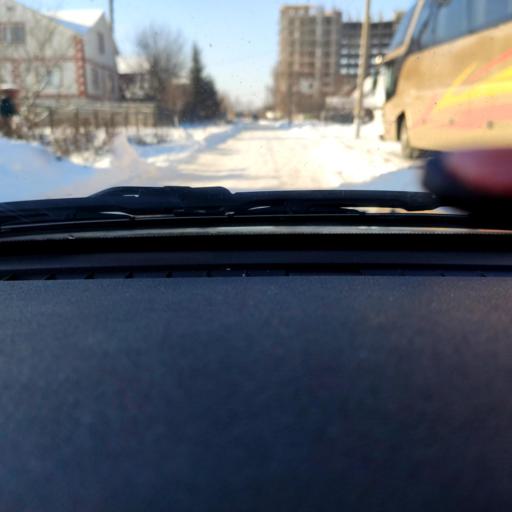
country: RU
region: Voronezj
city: Novaya Usman'
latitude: 51.6058
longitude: 39.3778
